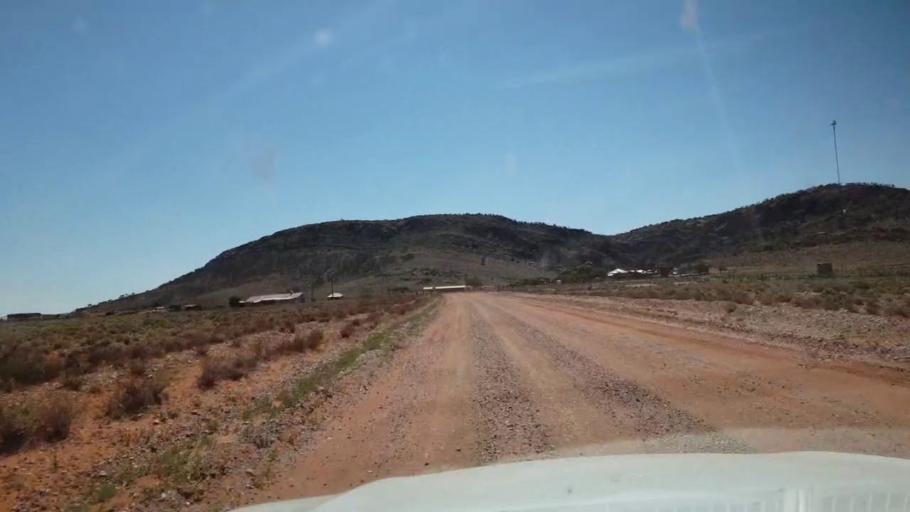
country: AU
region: South Australia
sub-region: Whyalla
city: Whyalla
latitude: -32.6881
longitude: 137.1270
